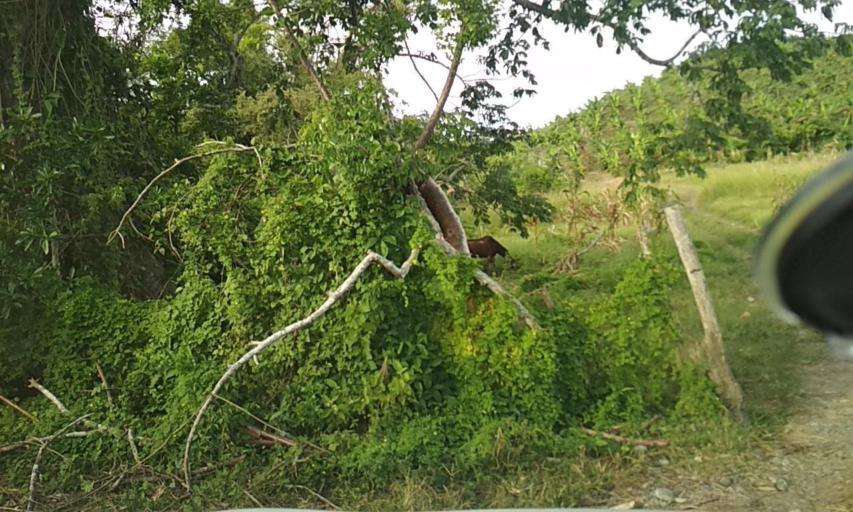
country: MX
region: Veracruz
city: Cazones de Herrera
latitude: 20.6521
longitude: -97.3368
